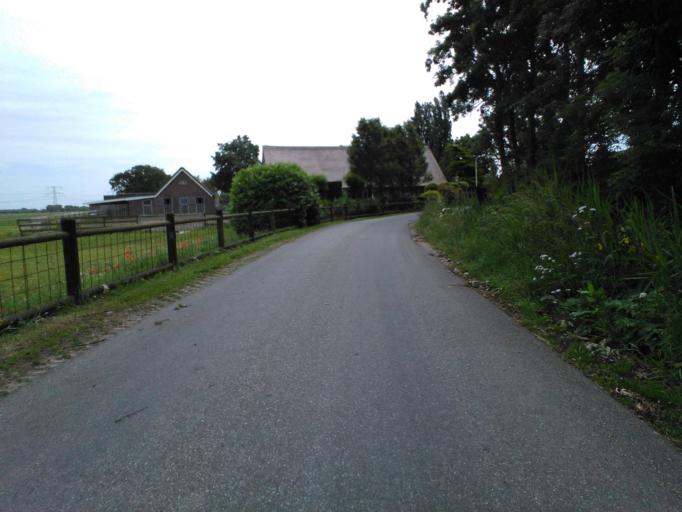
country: NL
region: South Holland
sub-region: Molenwaard
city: Nieuw-Lekkerland
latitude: 51.8666
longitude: 4.6927
